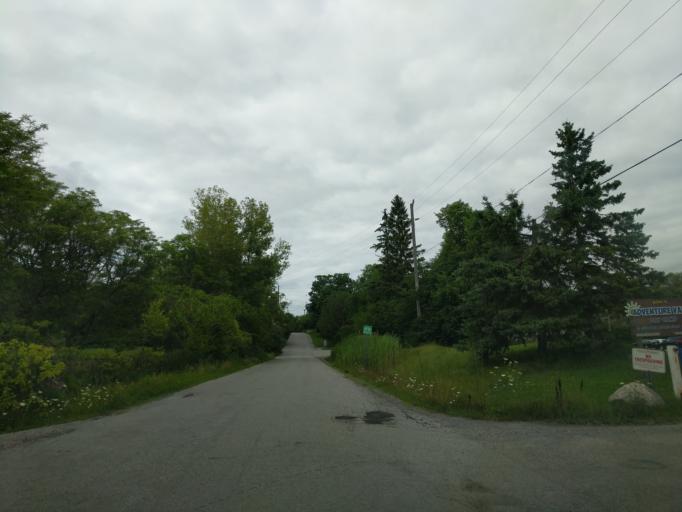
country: CA
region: Ontario
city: Willowdale
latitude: 43.8112
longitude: -79.3738
